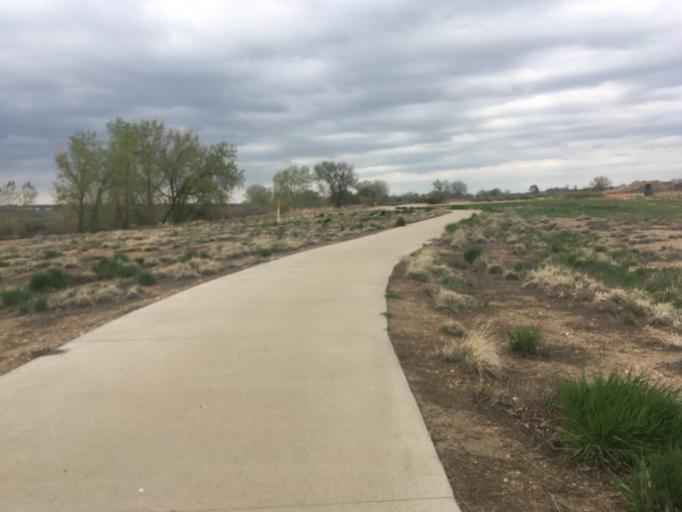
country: US
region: Colorado
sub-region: Weld County
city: Mead
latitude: 40.1751
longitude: -104.9759
